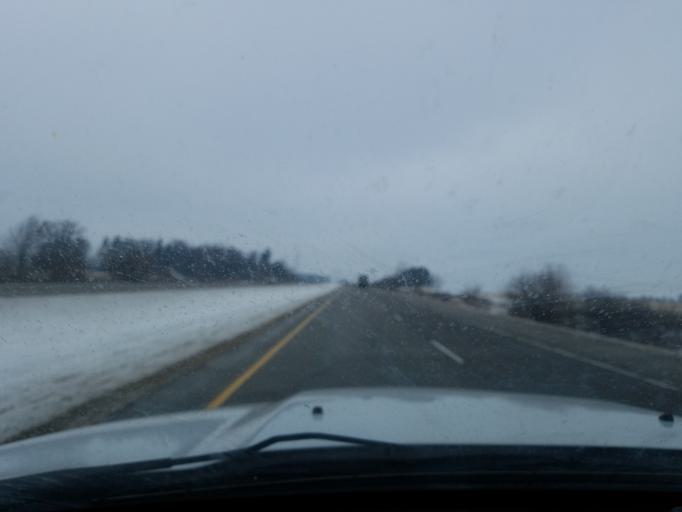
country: US
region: Indiana
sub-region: Marshall County
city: Argos
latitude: 41.1951
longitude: -86.2535
